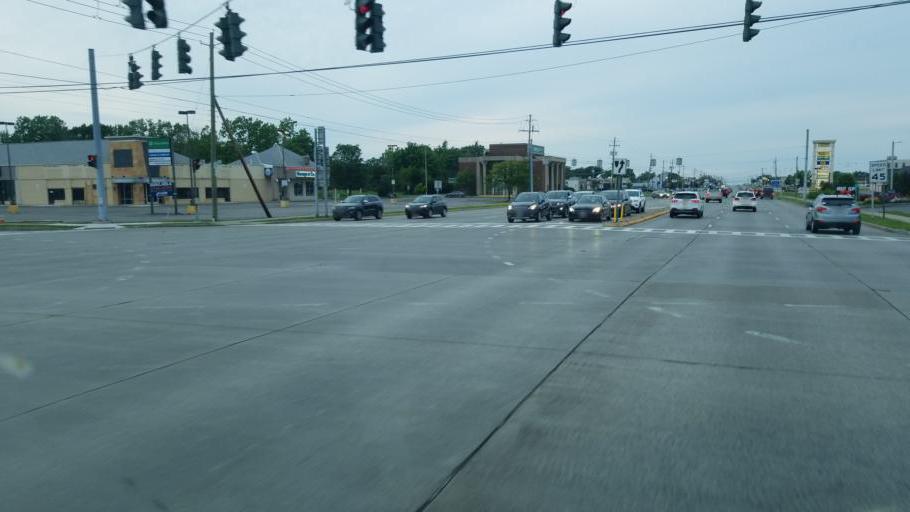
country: US
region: New York
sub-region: Erie County
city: Harris Hill
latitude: 42.9651
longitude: -78.6967
